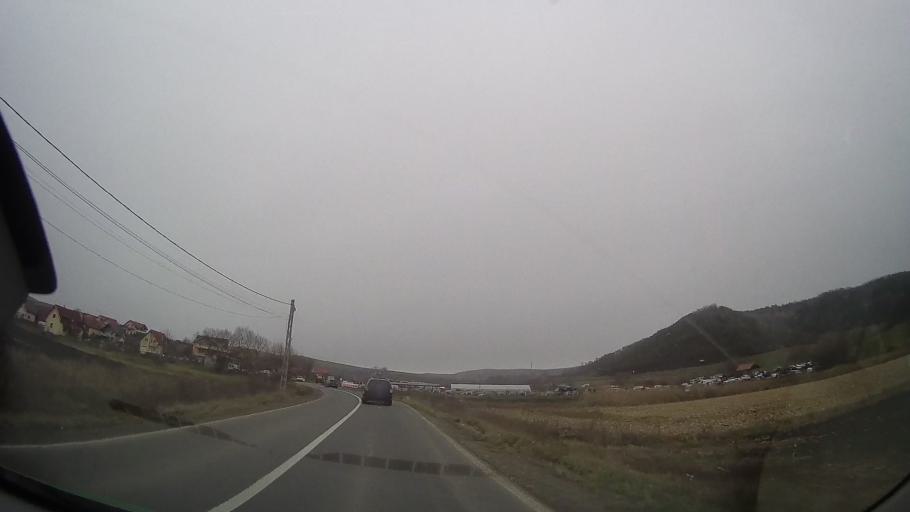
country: RO
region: Mures
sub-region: Comuna Ceausu de Campie
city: Ceausu de Campie
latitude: 46.6309
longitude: 24.5193
